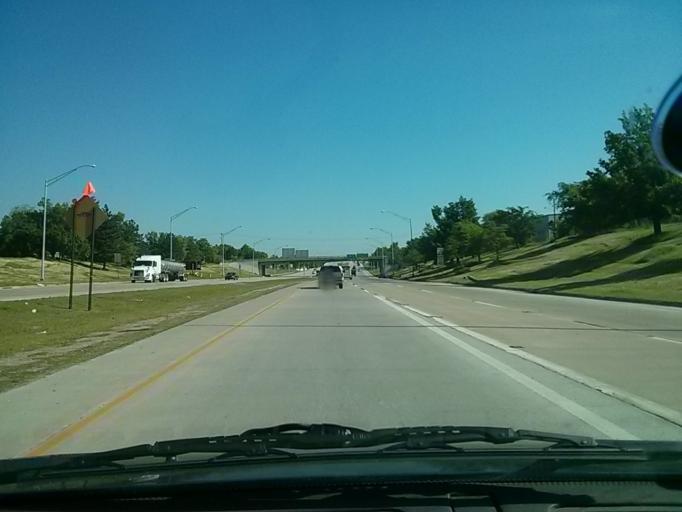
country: US
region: Oklahoma
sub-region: Tulsa County
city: Tulsa
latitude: 36.1640
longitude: -95.9806
